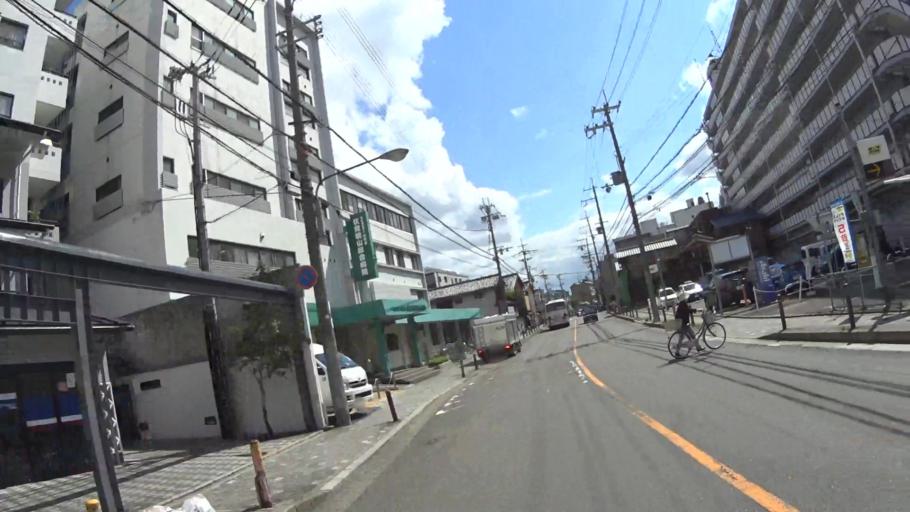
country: JP
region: Kyoto
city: Uji
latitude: 34.9323
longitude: 135.7586
